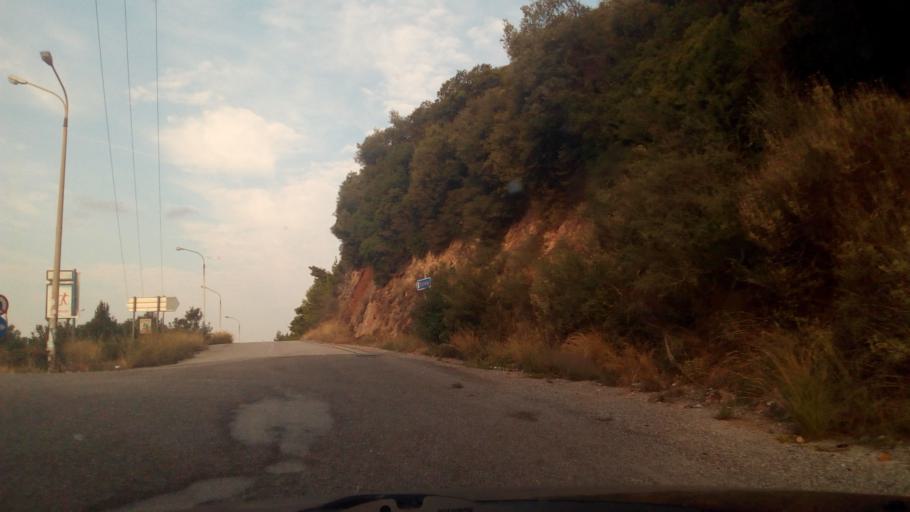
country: GR
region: West Greece
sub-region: Nomos Aitolias kai Akarnanias
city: Nafpaktos
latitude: 38.4085
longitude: 21.9460
